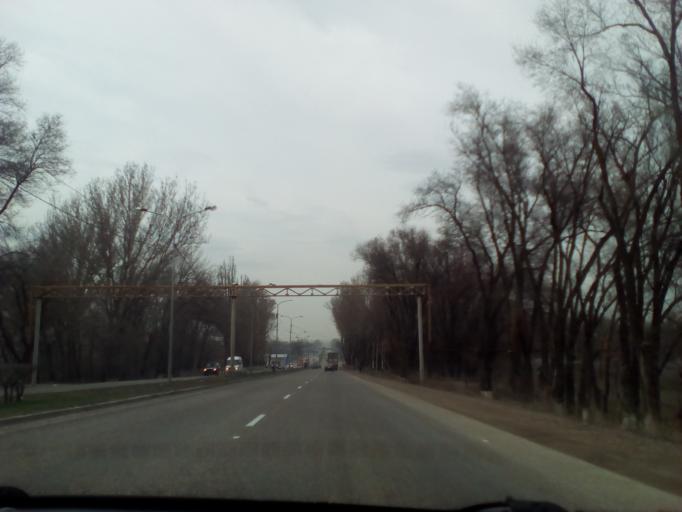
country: KZ
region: Almaty Oblysy
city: Burunday
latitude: 43.2168
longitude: 76.6589
